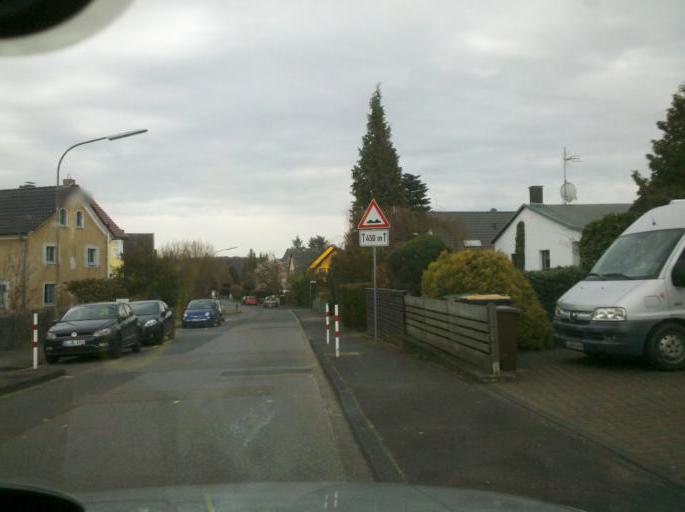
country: DE
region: North Rhine-Westphalia
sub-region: Regierungsbezirk Koln
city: Rosrath
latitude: 50.9001
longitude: 7.1760
